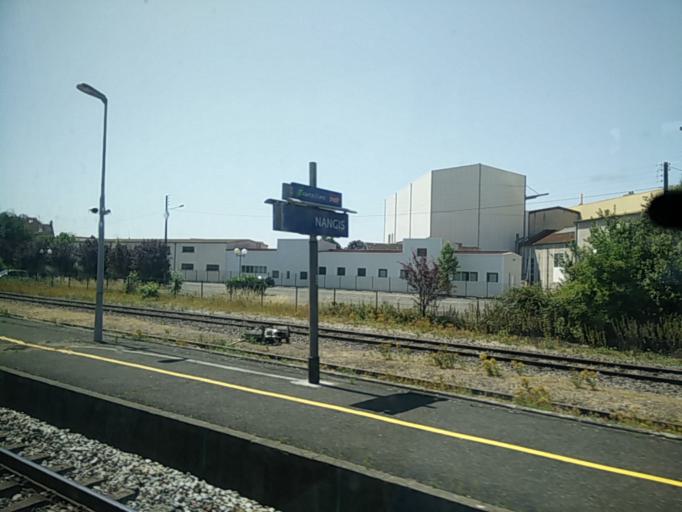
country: FR
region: Ile-de-France
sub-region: Departement de Seine-et-Marne
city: Nangis
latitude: 48.5628
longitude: 3.0110
